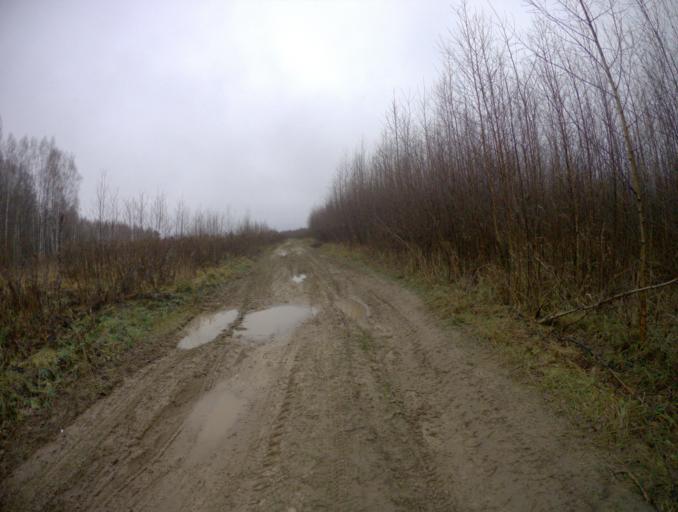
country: RU
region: Vladimir
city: Golovino
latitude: 55.9895
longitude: 40.4461
